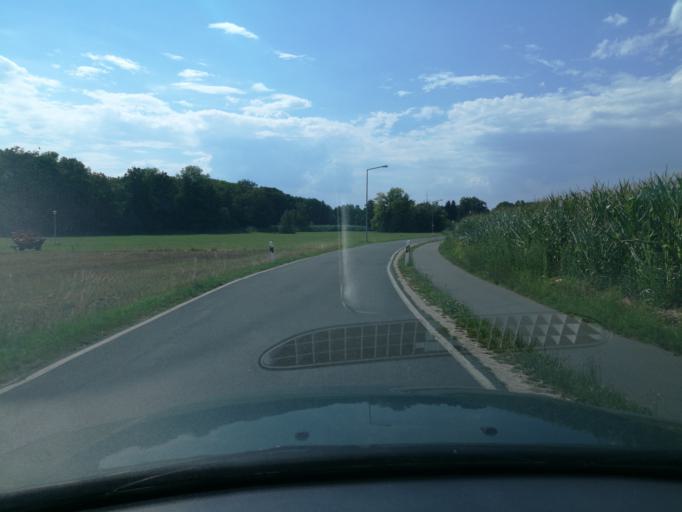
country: DE
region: Bavaria
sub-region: Regierungsbezirk Mittelfranken
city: Furth
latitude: 49.5307
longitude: 11.0082
